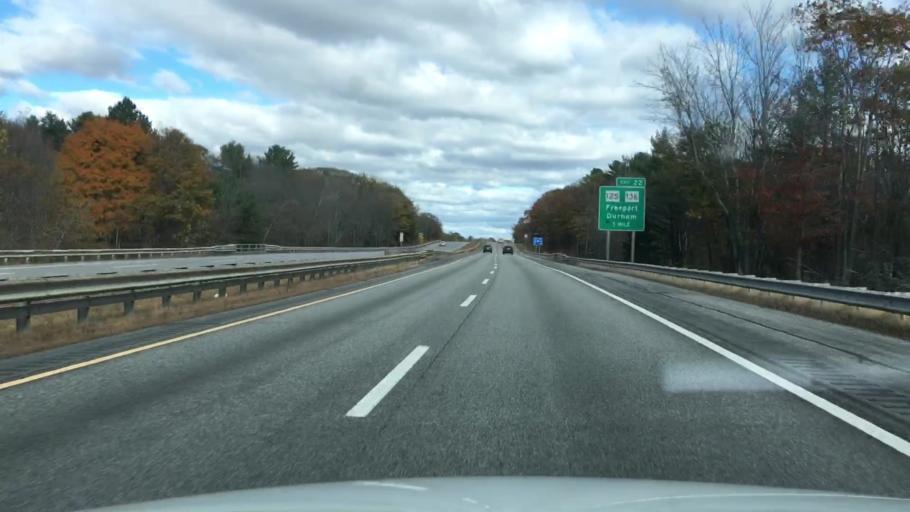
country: US
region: Maine
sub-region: Cumberland County
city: Freeport
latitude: 43.8513
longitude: -70.1150
